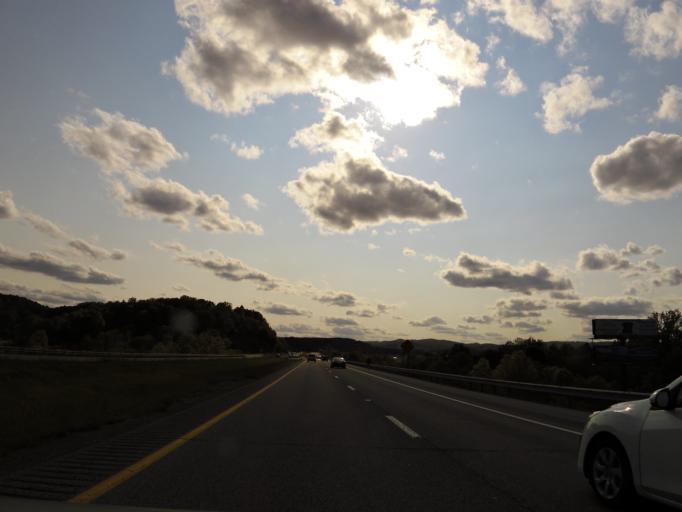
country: US
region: West Virginia
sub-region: Mercer County
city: Princeton
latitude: 37.3604
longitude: -81.0832
